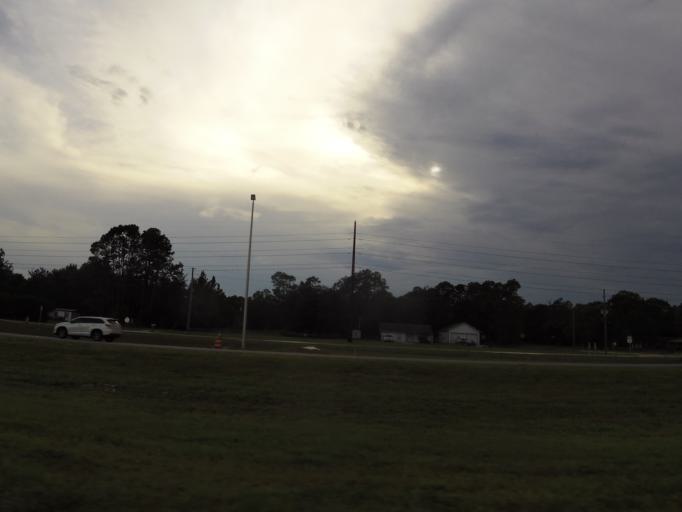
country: US
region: Florida
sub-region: Clay County
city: Lakeside
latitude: 30.1444
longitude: -81.8308
